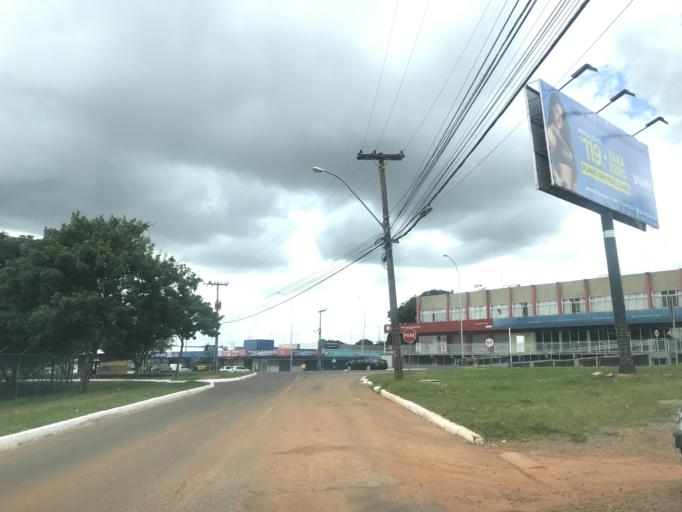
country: BR
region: Federal District
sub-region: Brasilia
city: Brasilia
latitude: -15.6500
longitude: -47.7885
